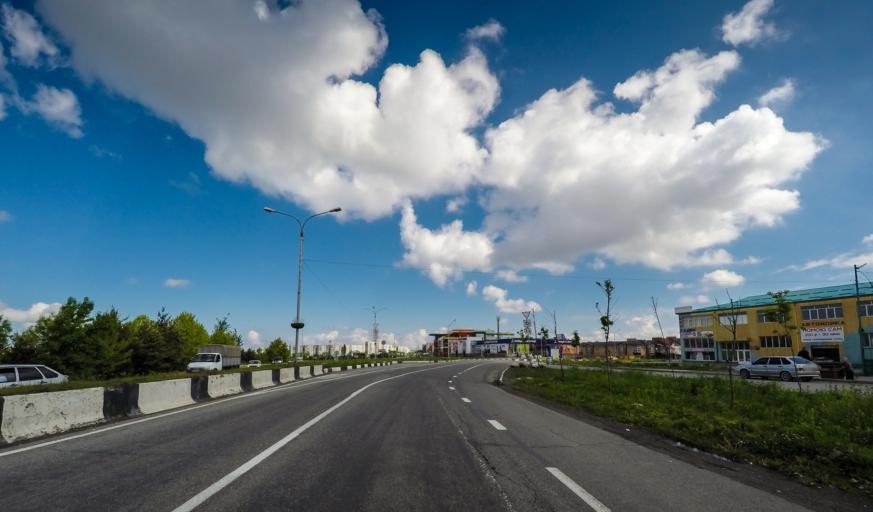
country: RU
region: North Ossetia
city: Vladikavkaz
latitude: 43.0307
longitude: 44.6430
